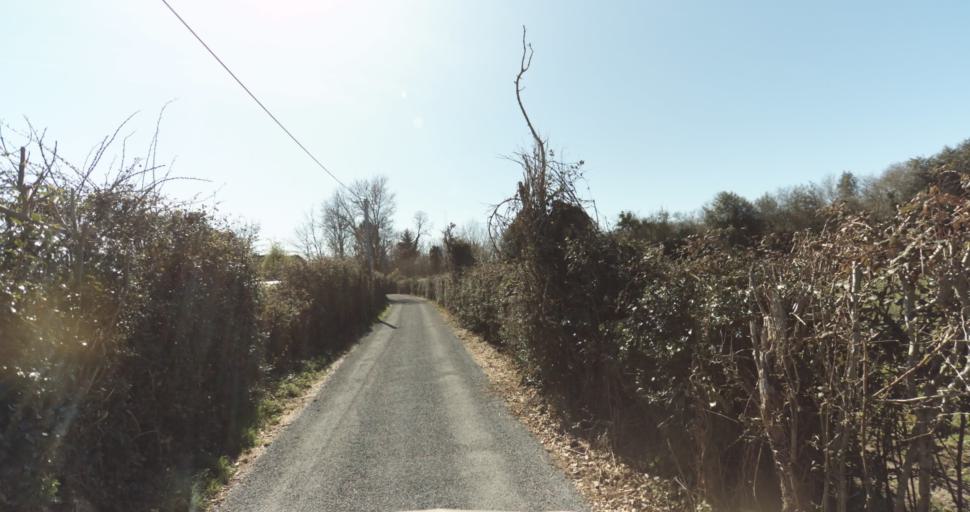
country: FR
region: Lower Normandy
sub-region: Departement du Calvados
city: Livarot
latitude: 48.9784
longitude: 0.0873
